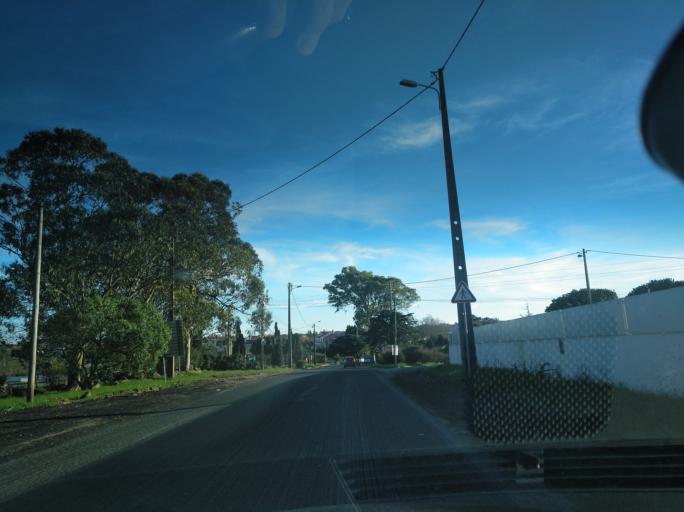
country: PT
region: Lisbon
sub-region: Sintra
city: Sintra
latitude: 38.8193
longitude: -9.3671
